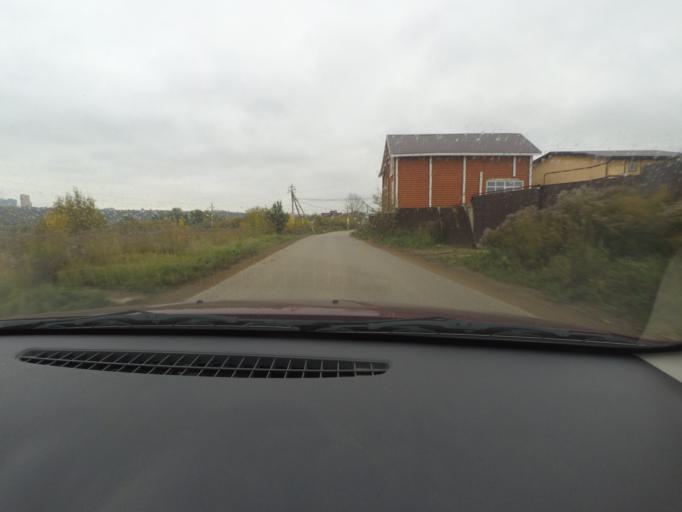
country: RU
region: Nizjnij Novgorod
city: Afonino
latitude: 56.2716
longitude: 44.0586
